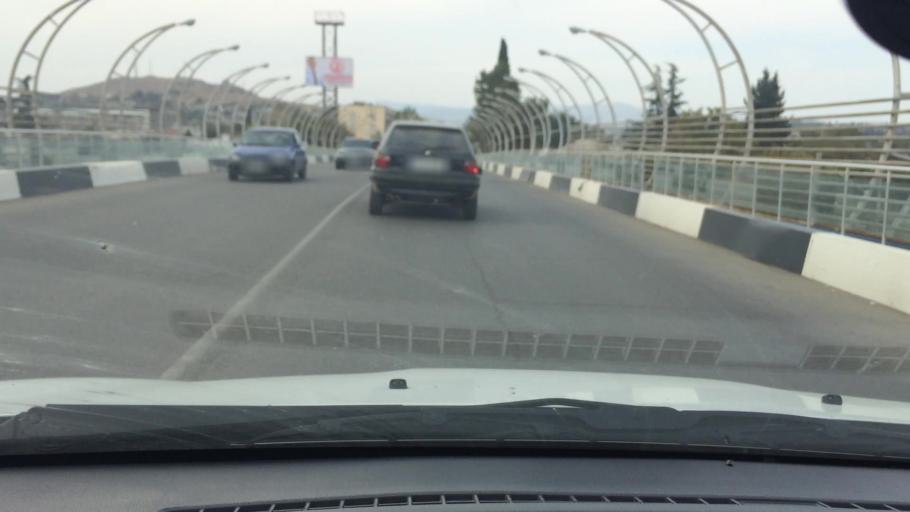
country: GE
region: Kvemo Kartli
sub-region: Marneuli
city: Marneuli
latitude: 41.4824
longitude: 44.8036
